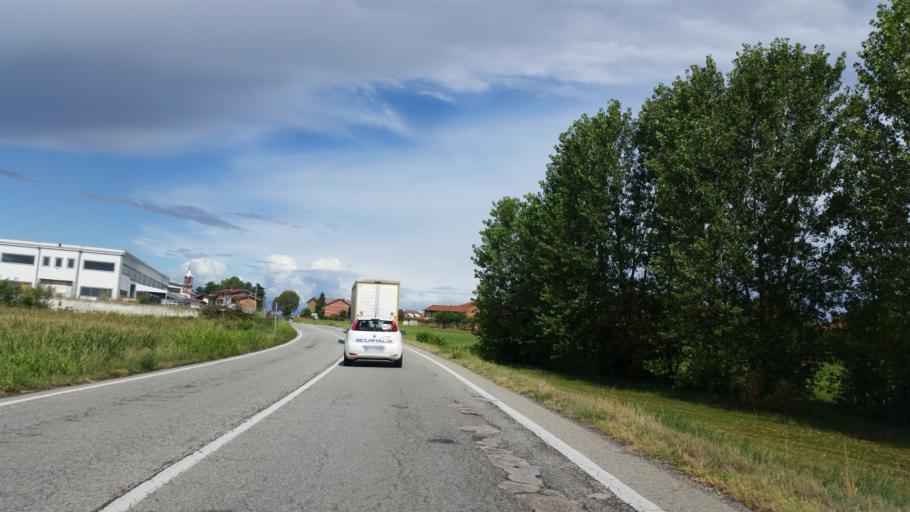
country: IT
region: Piedmont
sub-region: Provincia di Torino
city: Marocchi
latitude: 44.9367
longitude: 7.8272
